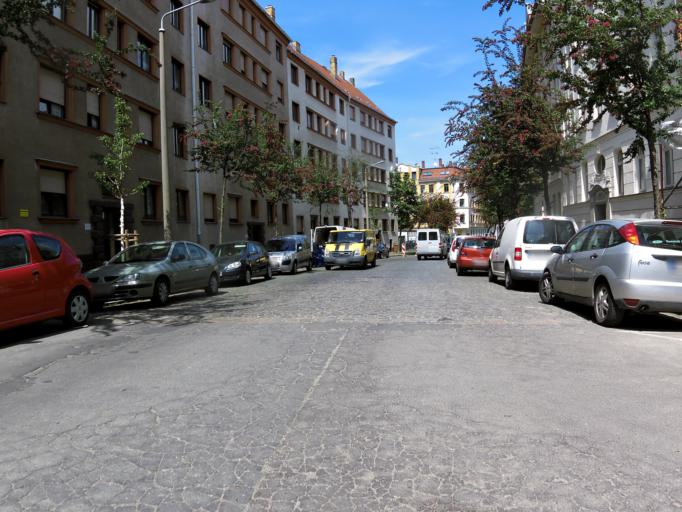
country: DE
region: Saxony
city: Leipzig
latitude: 51.3228
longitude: 12.4164
